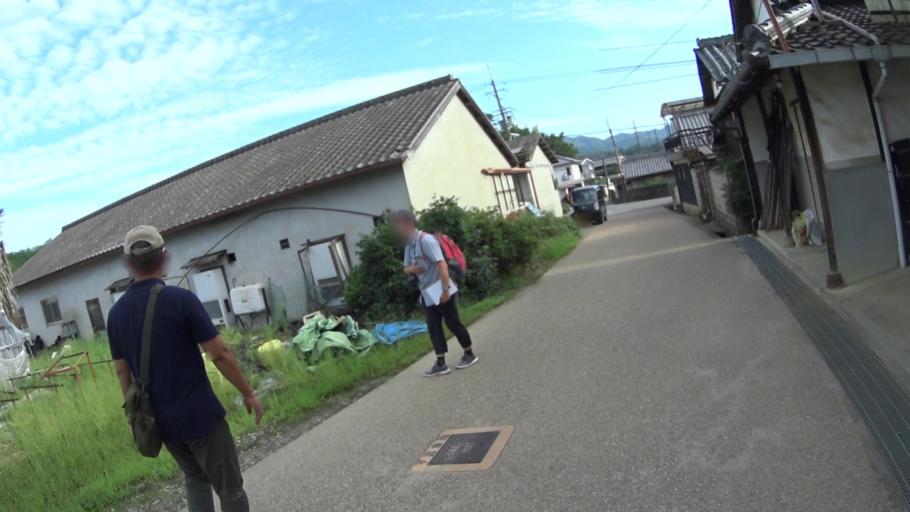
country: JP
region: Nara
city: Kashihara-shi
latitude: 34.4672
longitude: 135.8000
